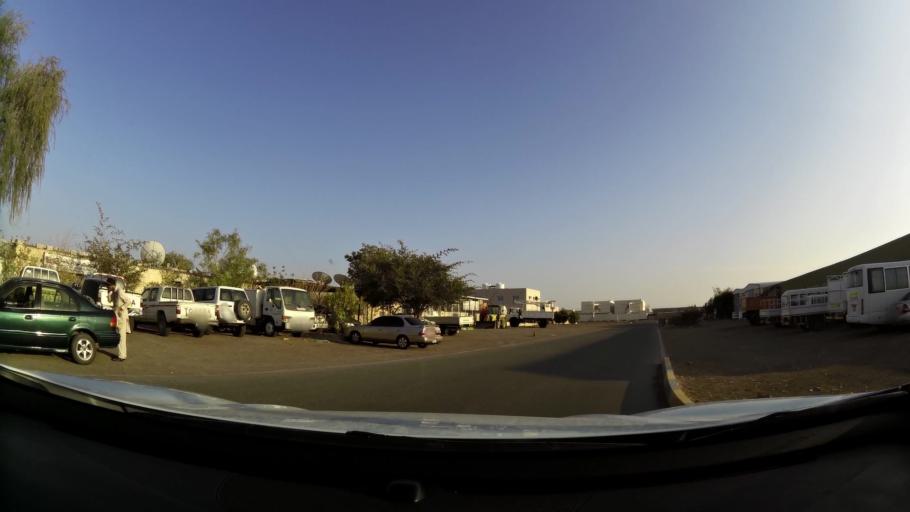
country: AE
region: Abu Dhabi
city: Al Ain
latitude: 24.1497
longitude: 55.8376
